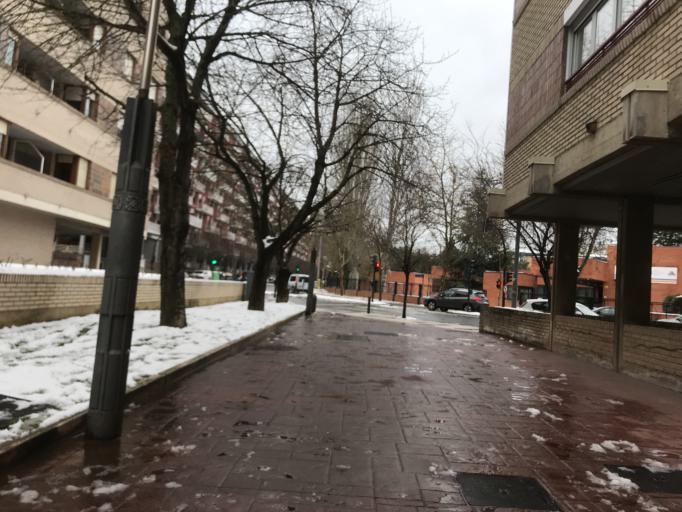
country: ES
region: Basque Country
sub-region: Provincia de Alava
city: Gasteiz / Vitoria
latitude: 42.8550
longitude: -2.6870
